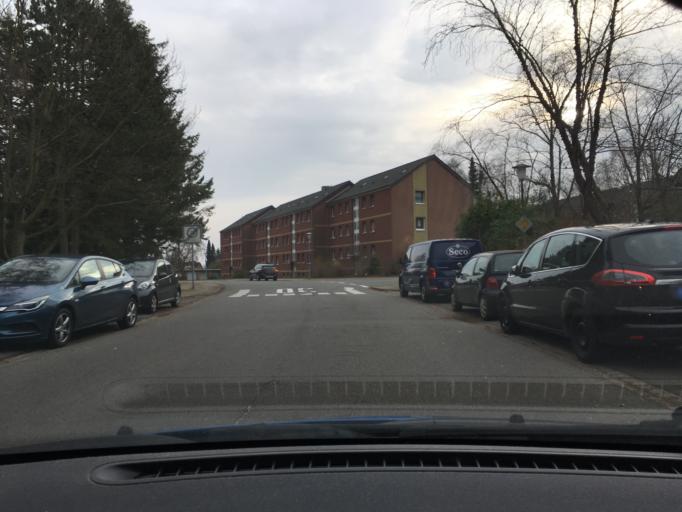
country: DE
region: Lower Saxony
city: Lueneburg
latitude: 53.2589
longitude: 10.3929
